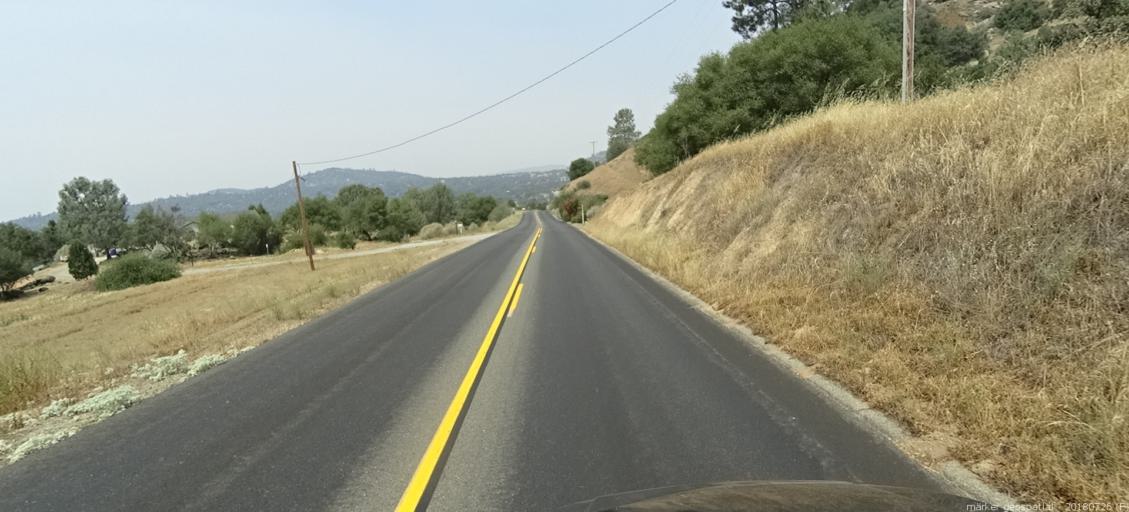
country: US
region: California
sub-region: Madera County
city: Coarsegold
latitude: 37.2493
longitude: -119.6970
